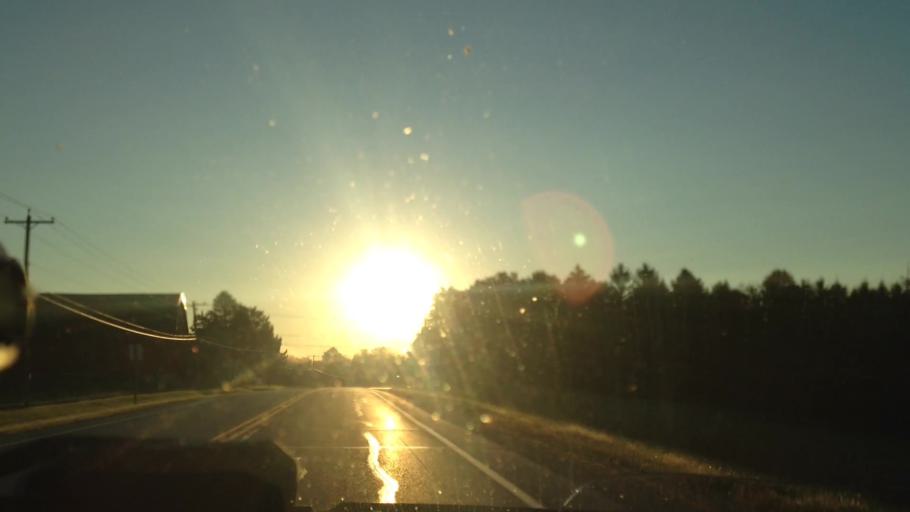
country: US
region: Wisconsin
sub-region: Washington County
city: Newburg
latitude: 43.4258
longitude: -88.0837
